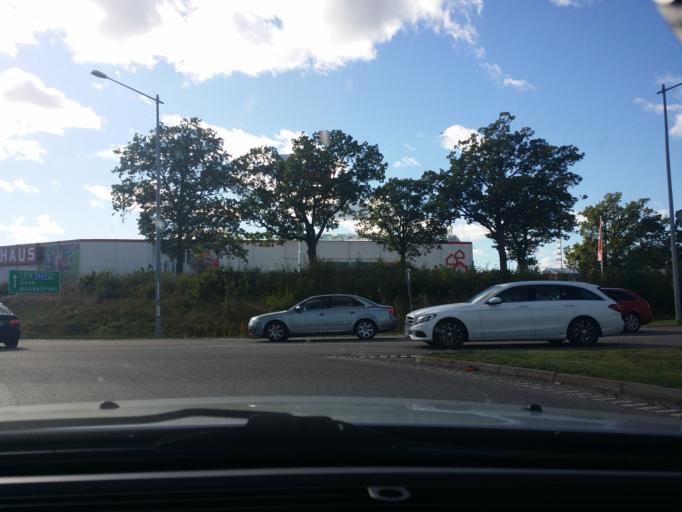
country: SE
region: Vaestmanland
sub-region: Vasteras
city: Vasteras
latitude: 59.6123
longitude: 16.4734
